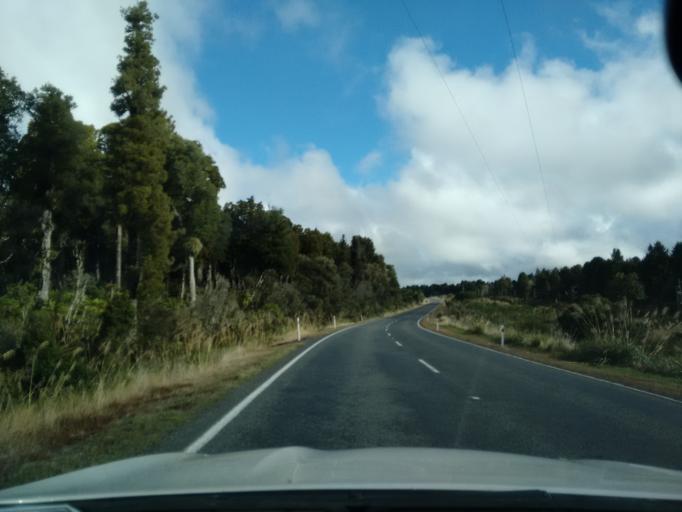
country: NZ
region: Manawatu-Wanganui
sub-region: Ruapehu District
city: Waiouru
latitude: -39.2431
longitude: 175.3916
